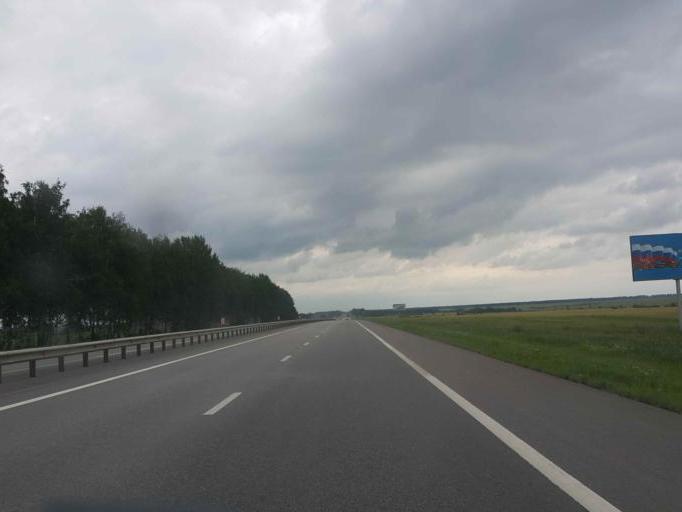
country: RU
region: Tambov
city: Selezni
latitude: 52.8221
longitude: 40.9209
